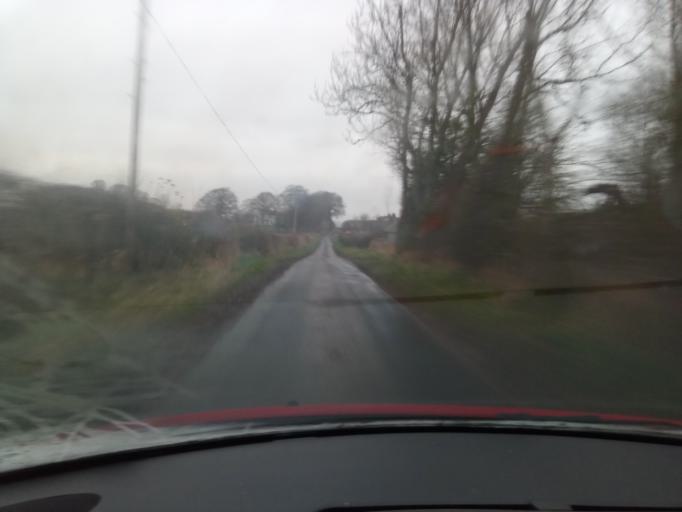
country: GB
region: Scotland
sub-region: The Scottish Borders
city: Kelso
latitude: 55.5671
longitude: -2.4398
